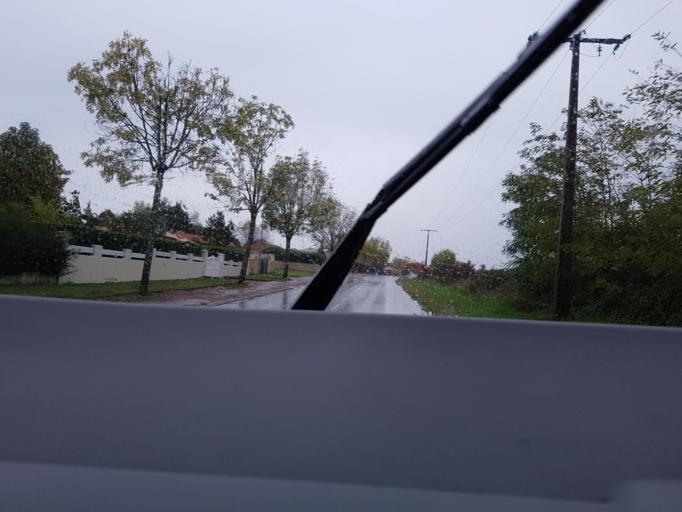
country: FR
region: Aquitaine
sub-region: Departement de la Gironde
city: Cubzac-les-Ponts
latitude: 44.9886
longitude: -0.4467
